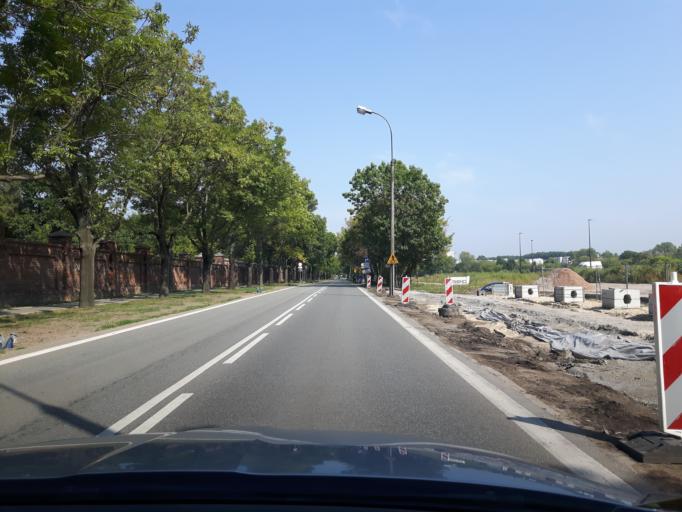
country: PL
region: Masovian Voivodeship
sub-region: Warszawa
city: Targowek
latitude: 52.2816
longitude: 21.0465
